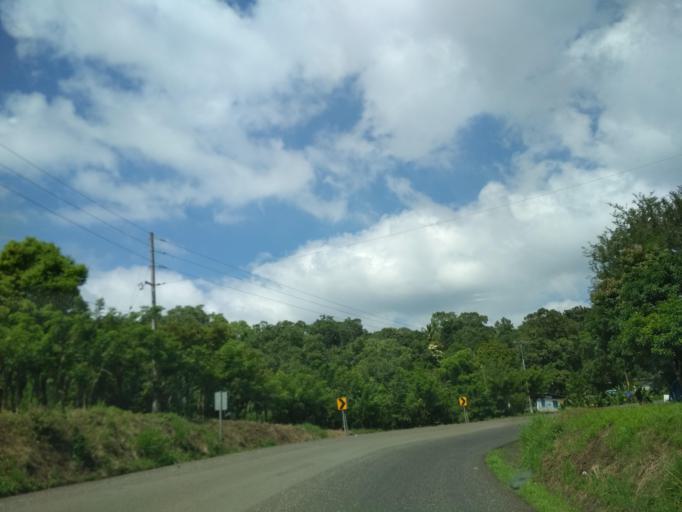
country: MX
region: Veracruz
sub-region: San Andres Tuxtla
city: Texcaltitan Xoteapan (Texcaltitan)
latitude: 18.4373
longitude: -95.2639
